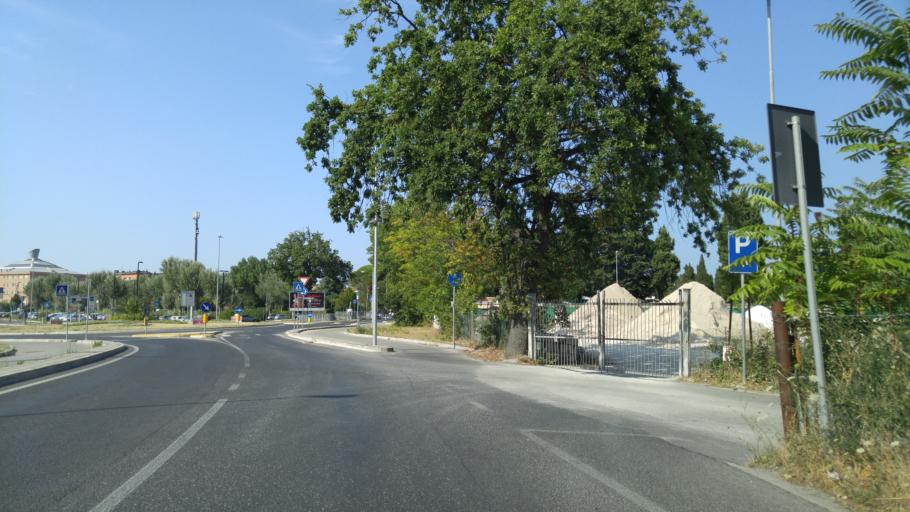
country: IT
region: The Marches
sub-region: Provincia di Pesaro e Urbino
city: Pesaro
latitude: 43.9015
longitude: 12.9137
